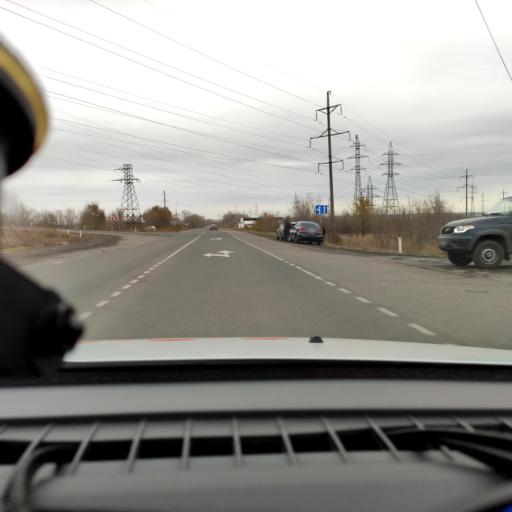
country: RU
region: Samara
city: Samara
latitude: 53.1153
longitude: 50.2245
